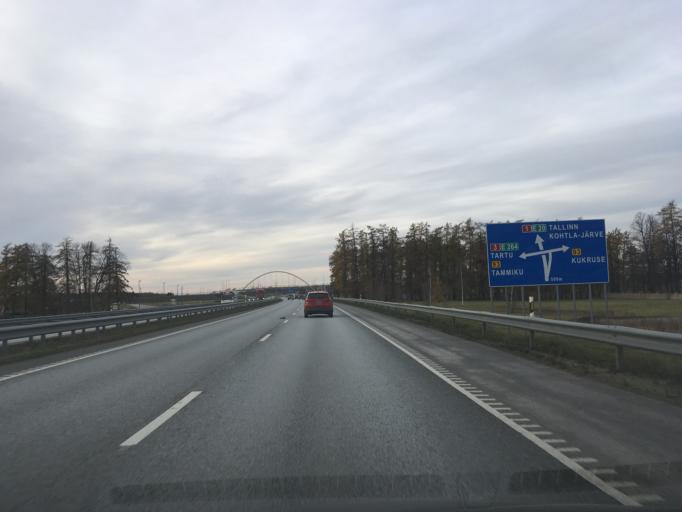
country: EE
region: Ida-Virumaa
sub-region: Johvi vald
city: Johvi
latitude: 59.3828
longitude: 27.3635
